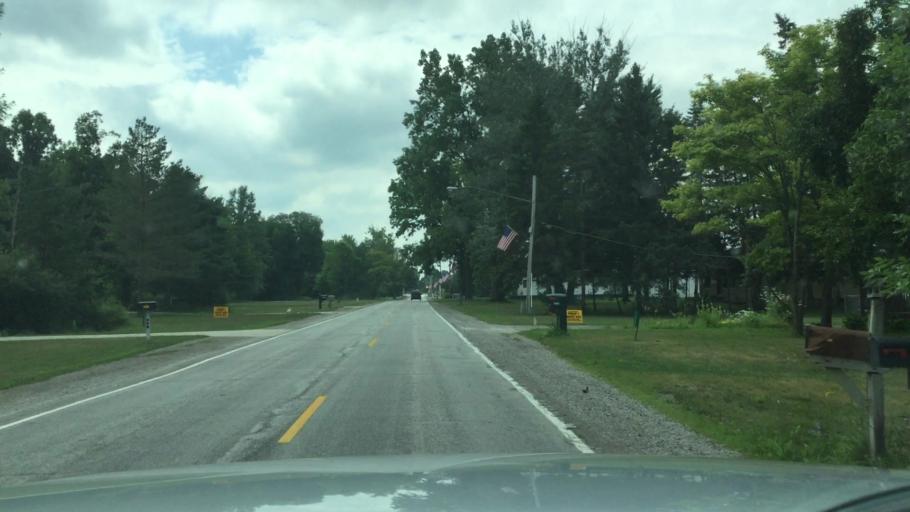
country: US
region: Michigan
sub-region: Saginaw County
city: Birch Run
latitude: 43.2567
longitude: -83.7943
